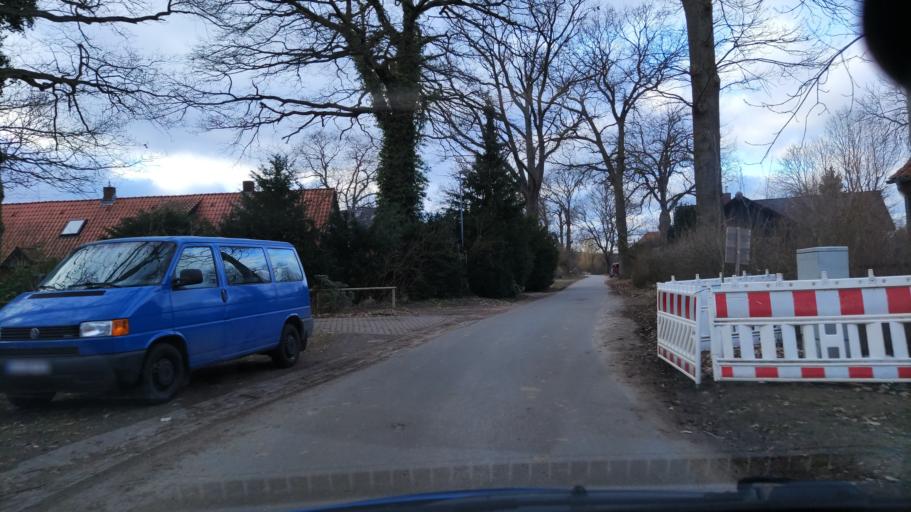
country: DE
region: Lower Saxony
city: Gohrde
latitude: 53.1580
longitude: 10.8807
